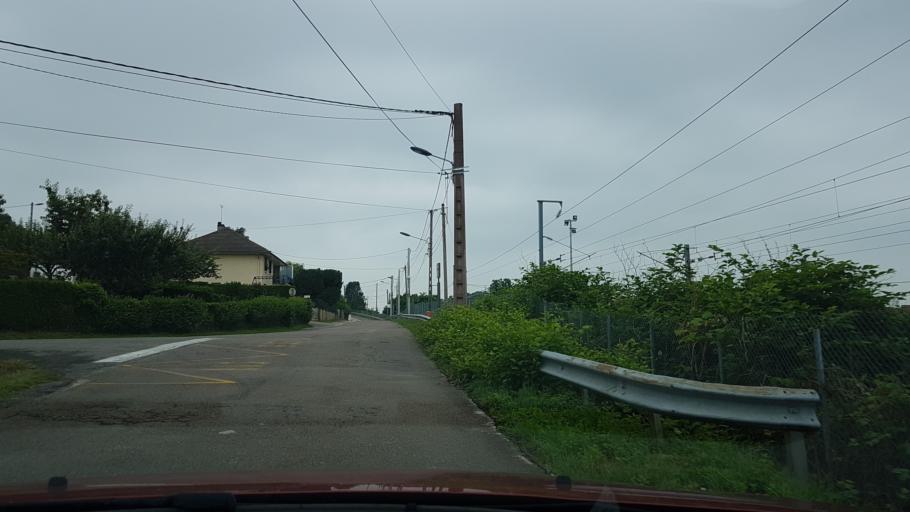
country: FR
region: Franche-Comte
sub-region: Departement du Jura
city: Lons-le-Saunier
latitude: 46.6701
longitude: 5.5418
